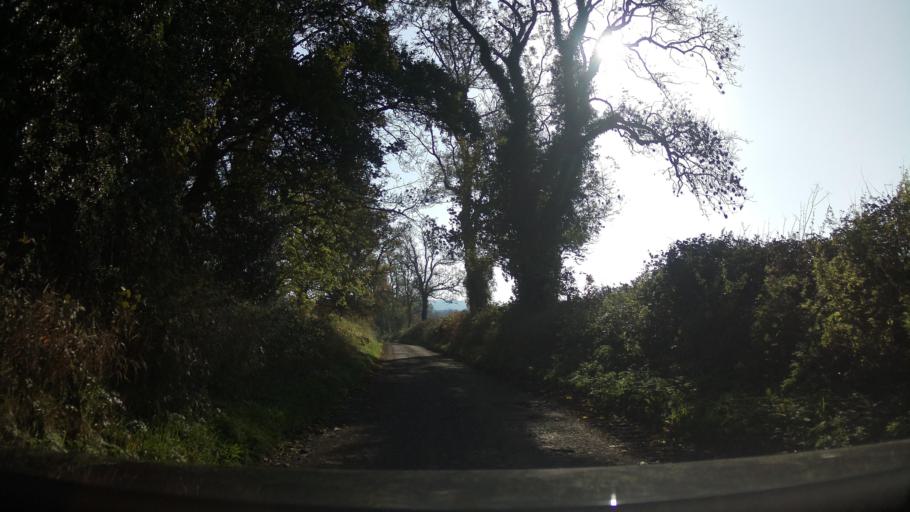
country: GB
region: England
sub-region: Somerset
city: Castle Cary
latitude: 51.0532
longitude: -2.4832
